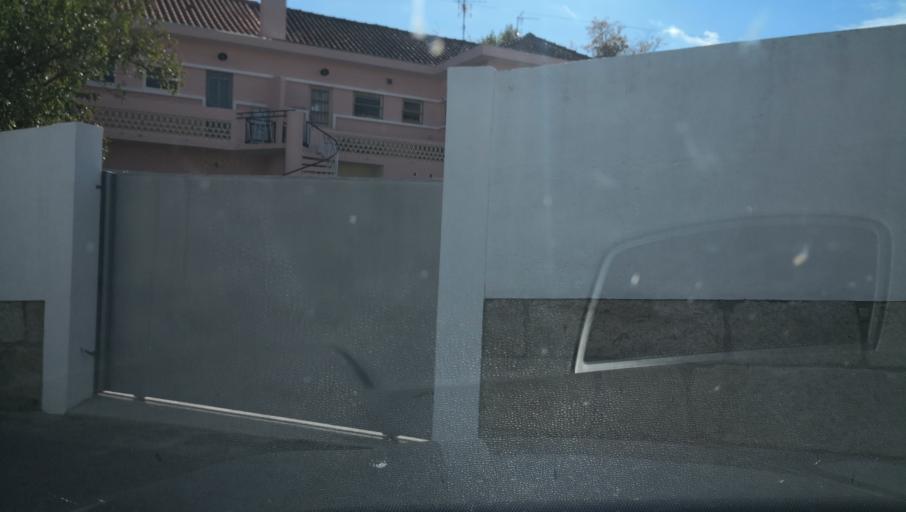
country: PT
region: Vila Real
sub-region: Chaves
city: Chaves
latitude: 41.7376
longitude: -7.4768
